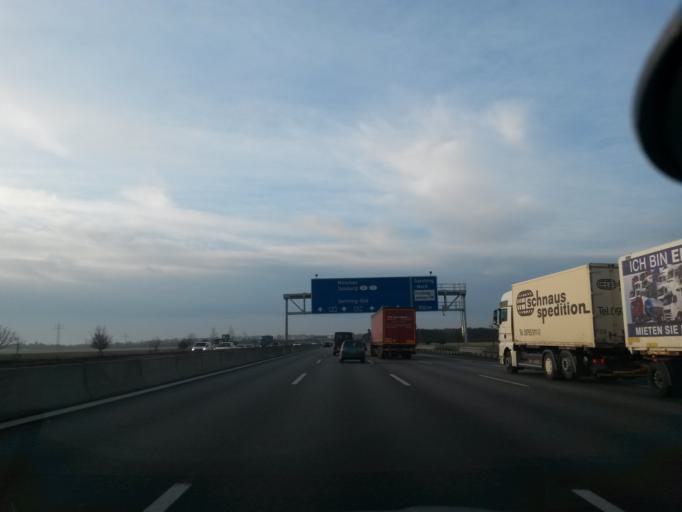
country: DE
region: Bavaria
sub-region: Upper Bavaria
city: Garching bei Munchen
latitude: 48.2733
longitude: 11.6433
